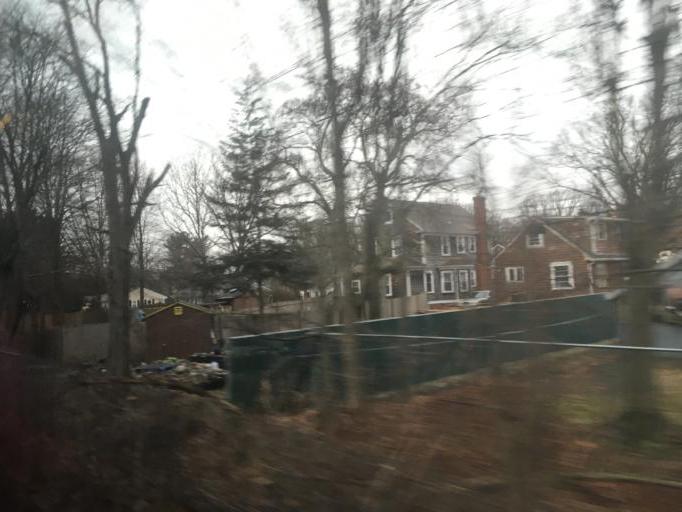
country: US
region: Massachusetts
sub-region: Bristol County
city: Attleboro
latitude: 41.9520
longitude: -71.2772
